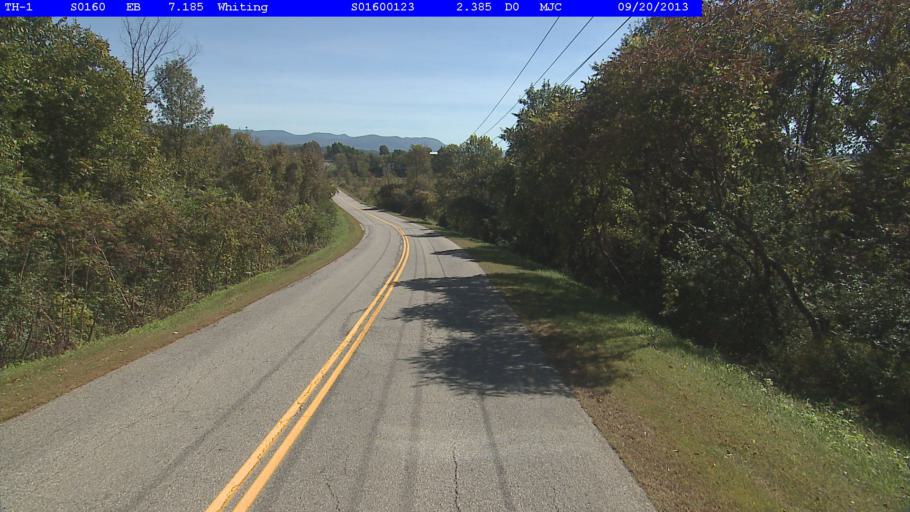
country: US
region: Vermont
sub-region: Rutland County
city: Brandon
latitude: 43.8552
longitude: -73.1825
